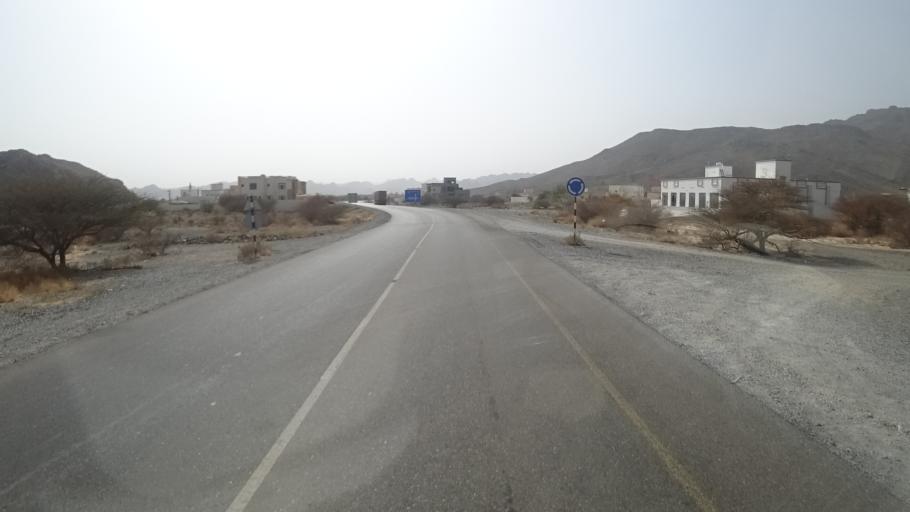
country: OM
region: Muhafazat ad Dakhiliyah
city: Nizwa
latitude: 23.0027
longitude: 57.5646
